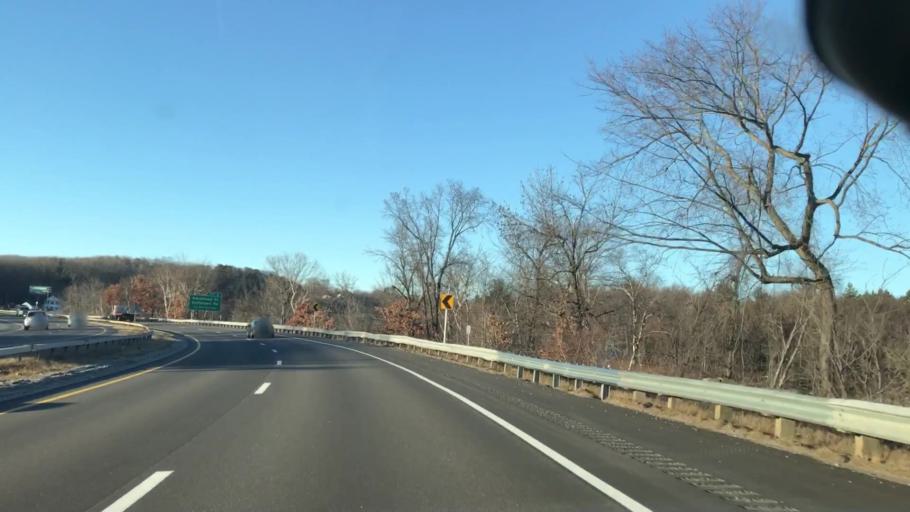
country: US
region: New Hampshire
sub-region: Hillsborough County
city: Manchester
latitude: 42.9967
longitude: -71.4711
